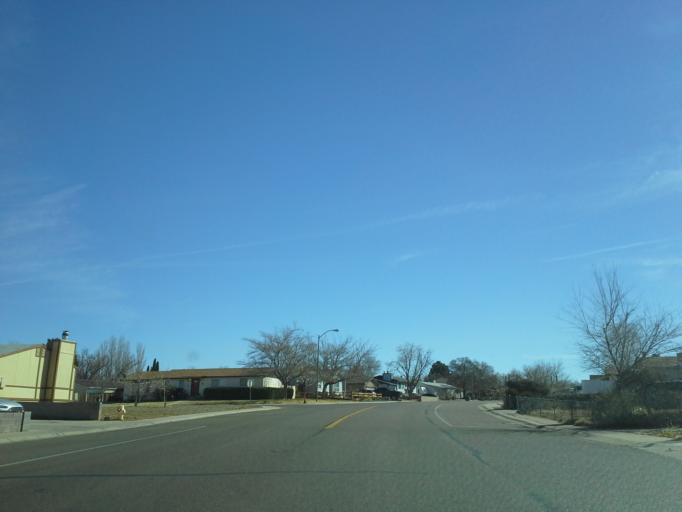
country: US
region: Arizona
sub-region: Coconino County
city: Page
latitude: 36.9255
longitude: -111.4583
